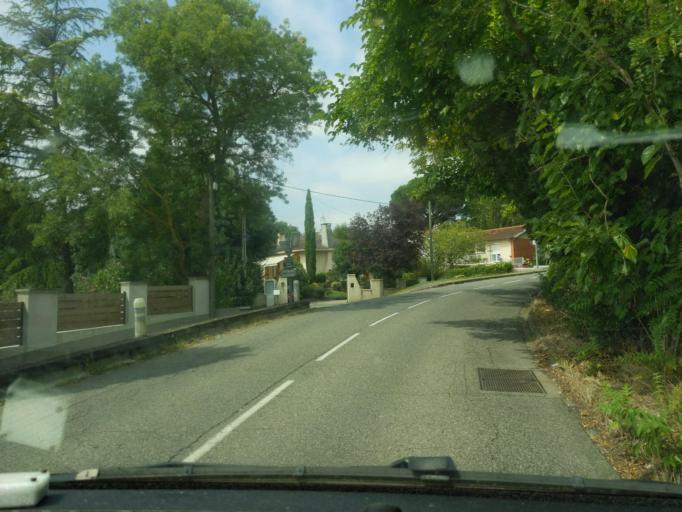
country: FR
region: Midi-Pyrenees
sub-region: Departement de la Haute-Garonne
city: Saint-Orens-de-Gameville
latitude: 43.5441
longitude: 1.5328
